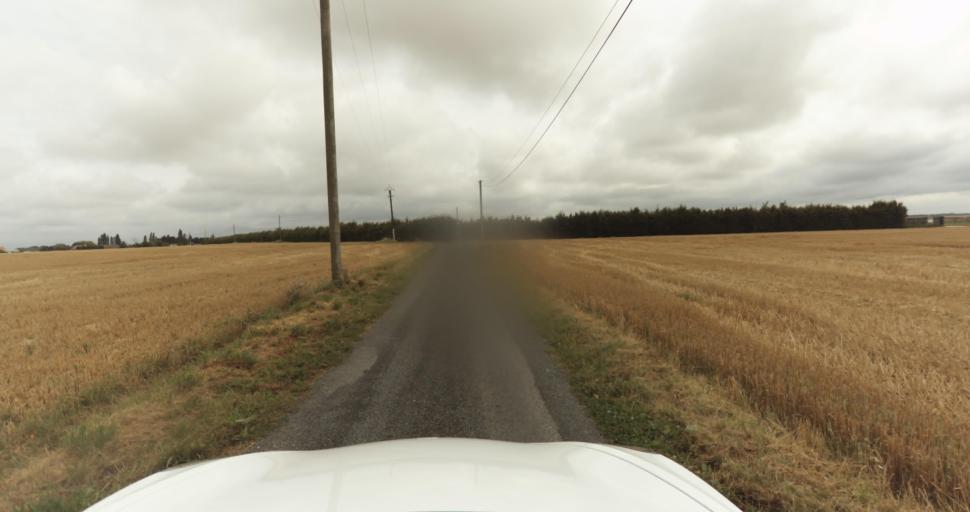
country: FR
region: Haute-Normandie
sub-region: Departement de l'Eure
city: Claville
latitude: 49.0627
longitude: 1.0381
